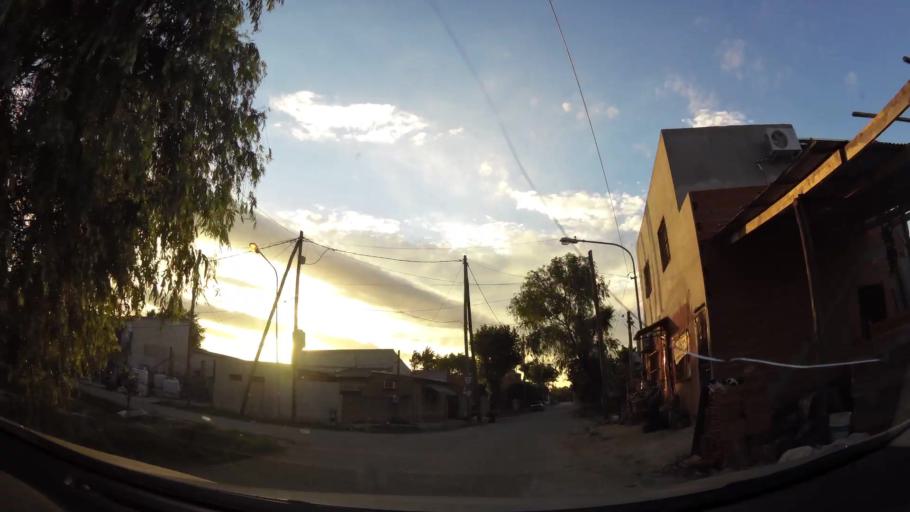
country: AR
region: Buenos Aires
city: Santa Catalina - Dique Lujan
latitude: -34.4407
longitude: -58.6604
